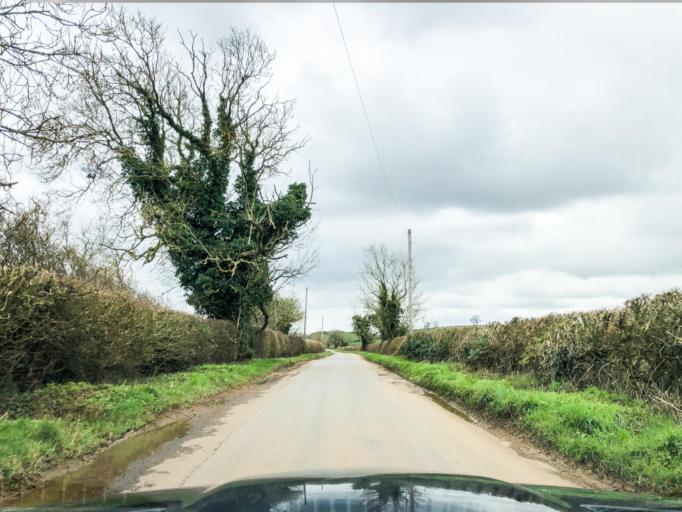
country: GB
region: England
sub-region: Oxfordshire
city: Hook Norton
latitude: 52.0788
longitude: -1.4773
